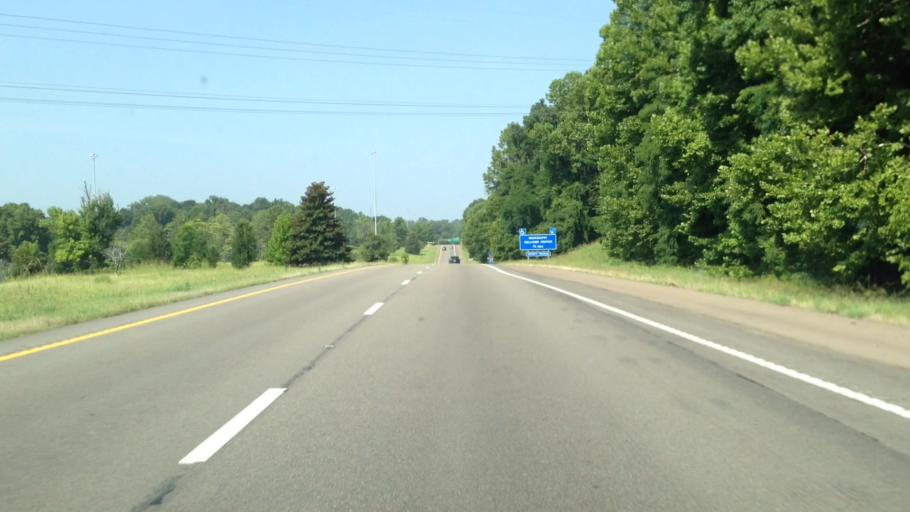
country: US
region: Mississippi
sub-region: Warren County
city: Vicksburg
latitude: 32.3149
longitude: -90.8862
